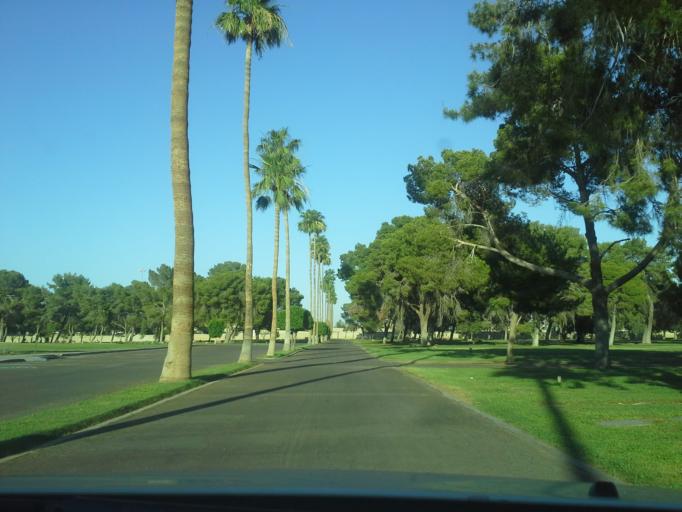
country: US
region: Arizona
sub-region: Maricopa County
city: Phoenix
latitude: 33.4586
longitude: -112.1116
